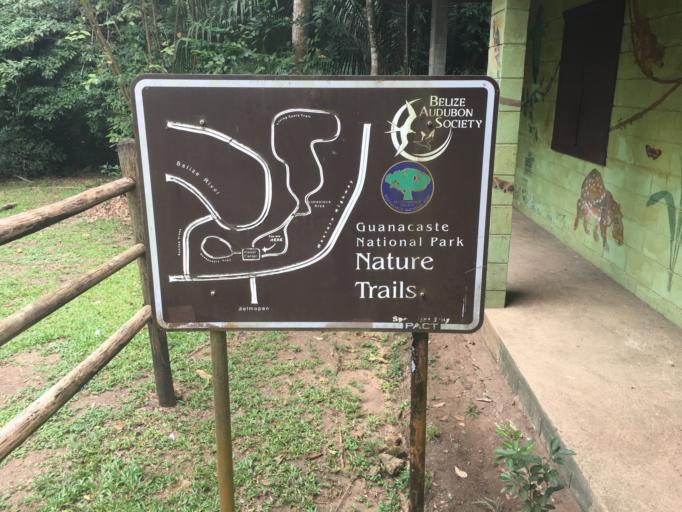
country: BZ
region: Cayo
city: Belmopan
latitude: 17.2617
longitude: -88.7879
